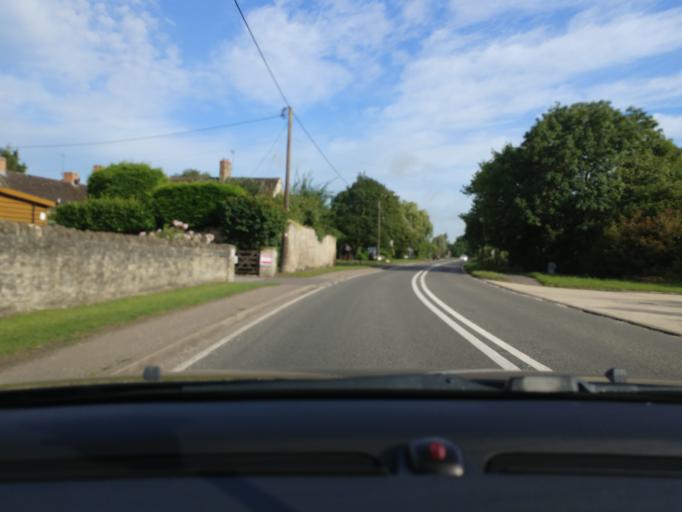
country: GB
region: England
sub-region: Oxfordshire
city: Kidlington
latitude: 51.8638
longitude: -1.2260
